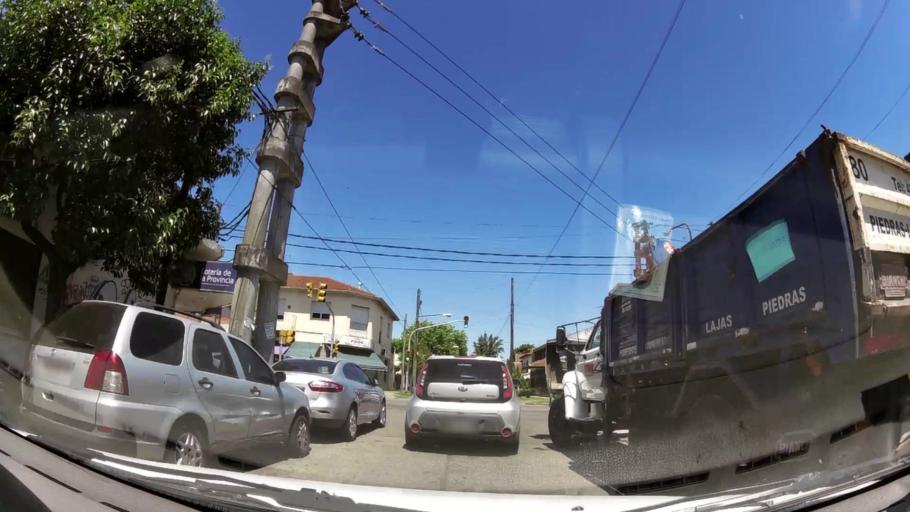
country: AR
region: Buenos Aires
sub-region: Partido de San Isidro
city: San Isidro
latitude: -34.5037
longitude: -58.5315
